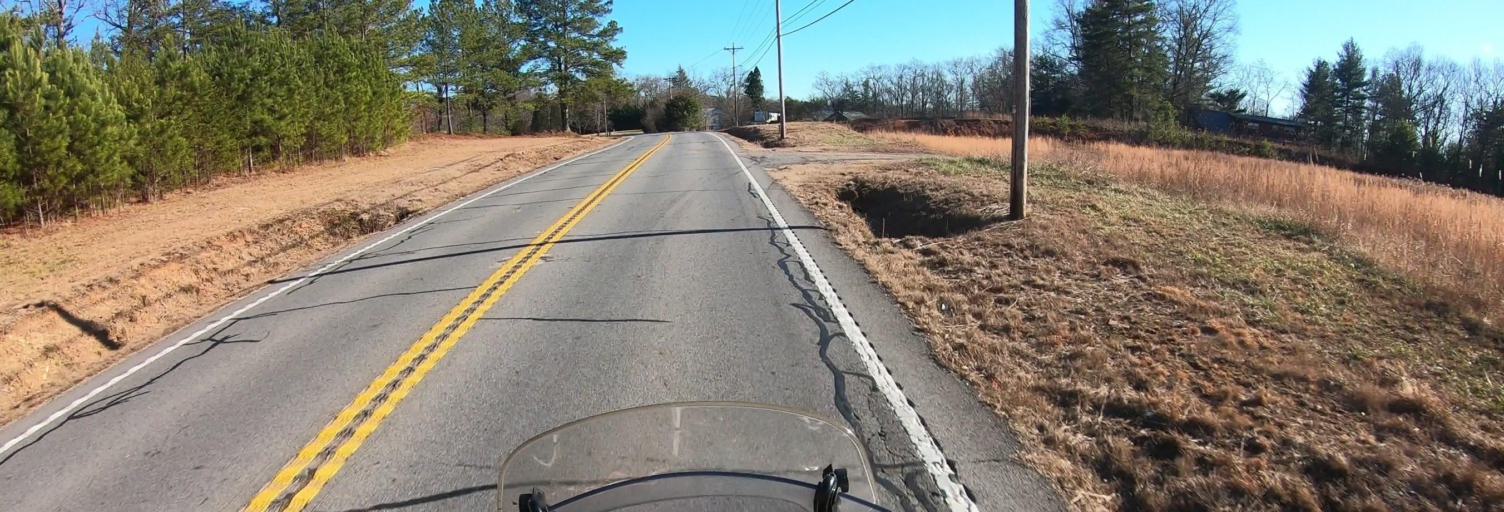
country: US
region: Georgia
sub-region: Fannin County
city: Blue Ridge
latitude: 34.9325
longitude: -84.3017
